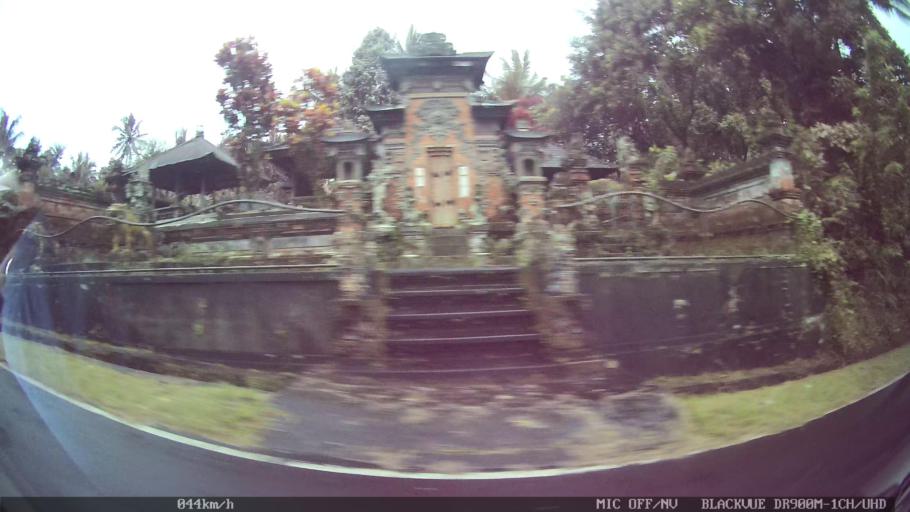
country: ID
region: Bali
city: Pegongan
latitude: -8.4923
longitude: 115.2374
